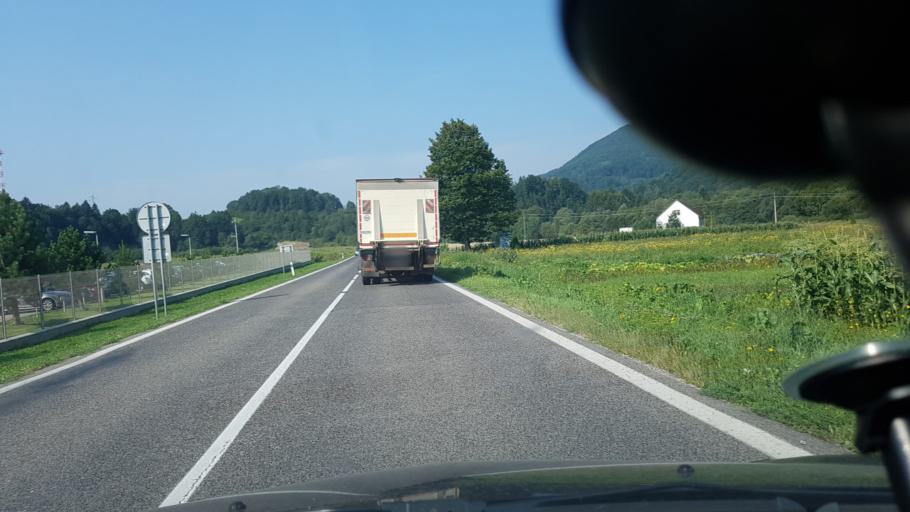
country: SK
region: Zilinsky
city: Tvrdosin
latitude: 49.2813
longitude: 19.4741
